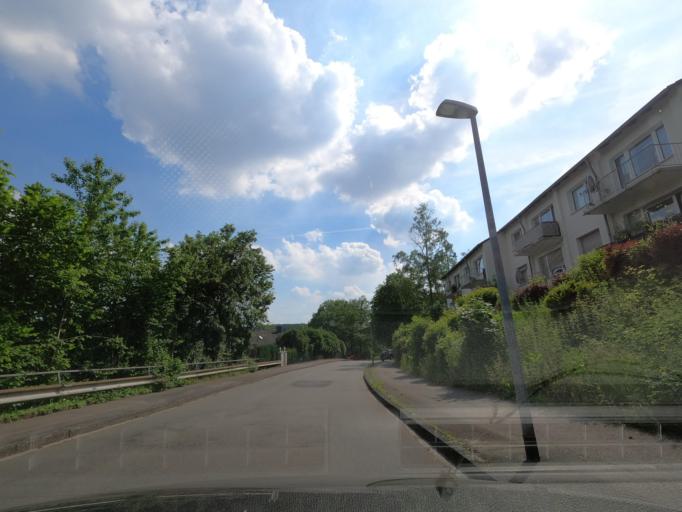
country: DE
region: North Rhine-Westphalia
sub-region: Regierungsbezirk Arnsberg
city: Luedenscheid
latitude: 51.2462
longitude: 7.6116
